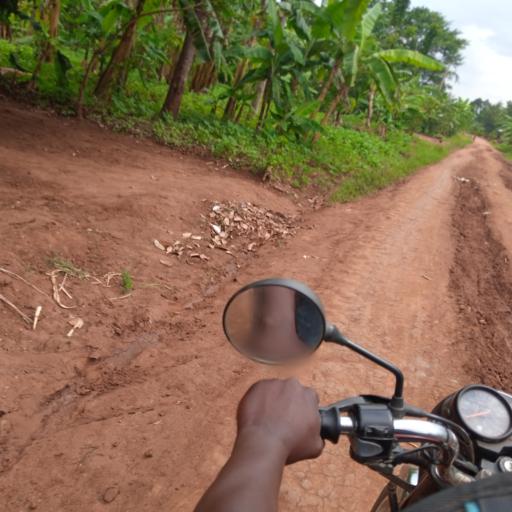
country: UG
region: Eastern Region
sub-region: Mbale District
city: Mbale
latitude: 1.1161
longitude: 34.1936
